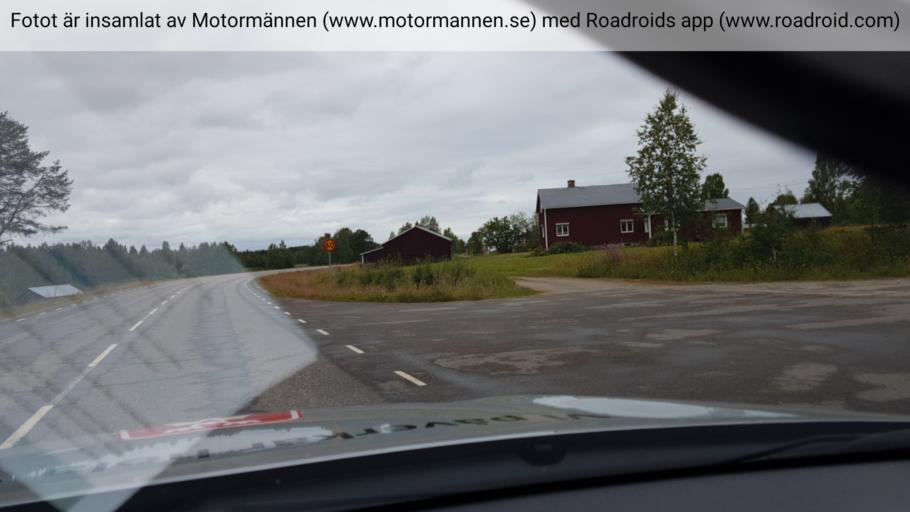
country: SE
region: Norrbotten
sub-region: Pajala Kommun
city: Pajala
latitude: 67.1619
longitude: 22.6304
